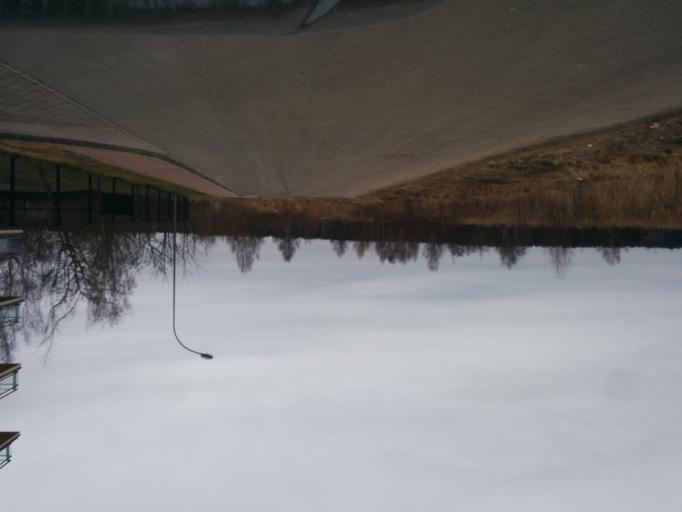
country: LV
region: Jurmala
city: Jurmala
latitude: 56.9613
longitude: 23.8195
